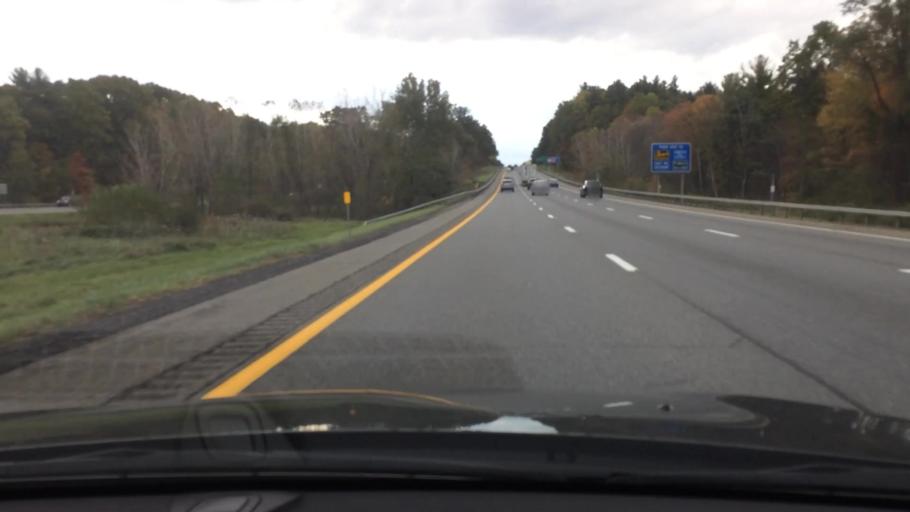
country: US
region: New York
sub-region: Saratoga County
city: Country Knolls
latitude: 42.9110
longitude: -73.7935
